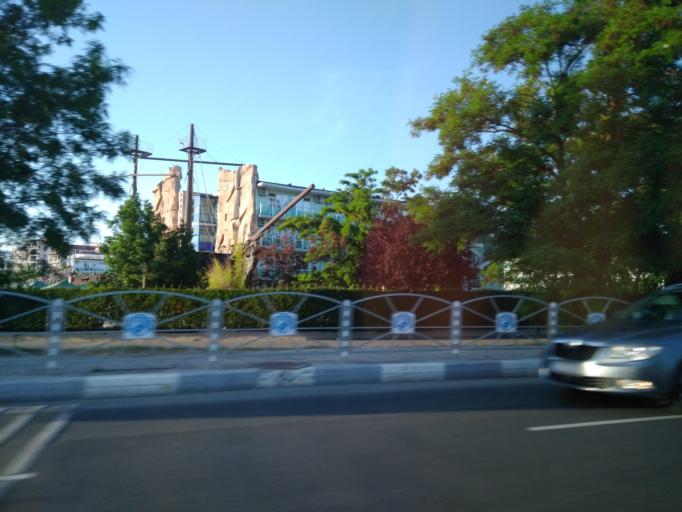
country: BG
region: Burgas
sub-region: Obshtina Nesebur
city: Nesebar
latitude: 42.6655
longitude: 27.7076
